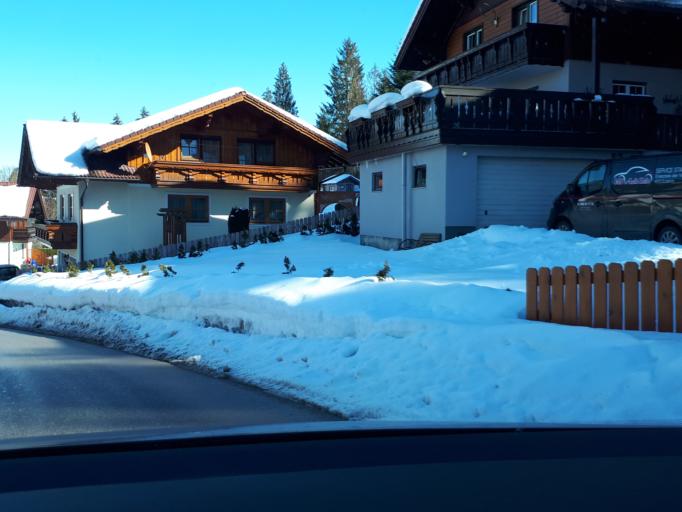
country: AT
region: Styria
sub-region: Politischer Bezirk Liezen
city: Pruggern
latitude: 47.4188
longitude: 13.8754
